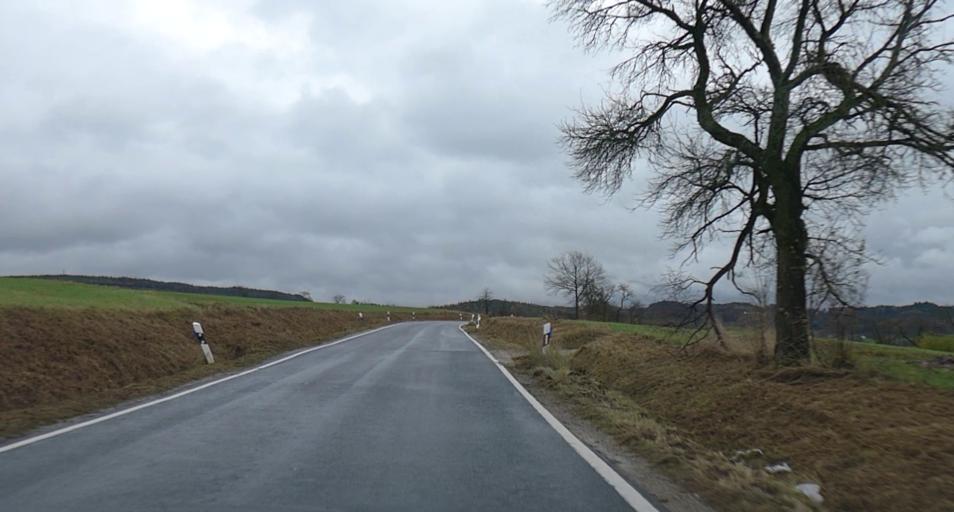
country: DE
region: Bavaria
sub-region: Upper Franconia
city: Kunreuth
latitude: 49.6853
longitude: 11.1525
